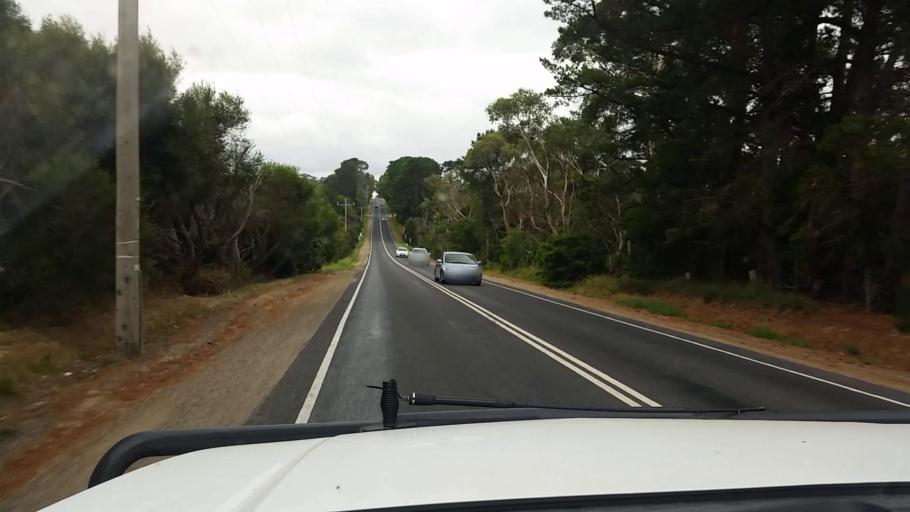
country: AU
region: Victoria
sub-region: Mornington Peninsula
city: Hastings
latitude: -38.2840
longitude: 145.1456
